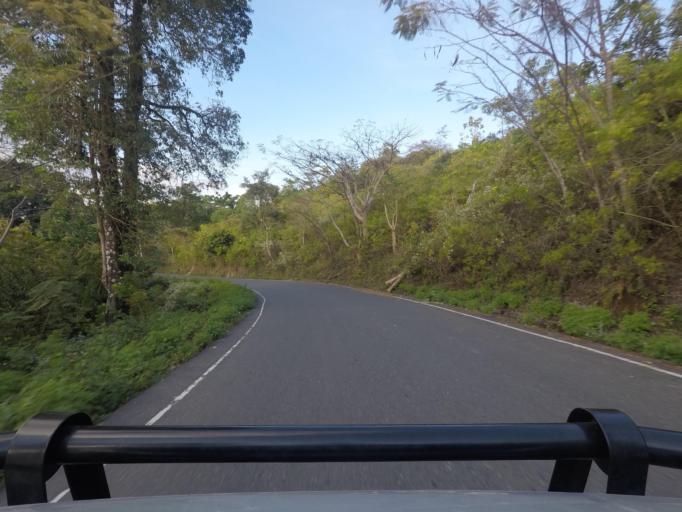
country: TL
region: Bobonaro
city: Maliana
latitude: -8.9579
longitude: 125.0637
